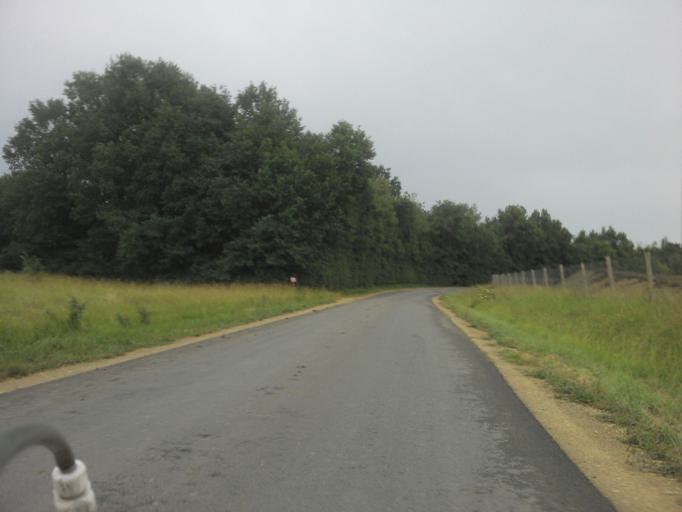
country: FR
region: Pays de la Loire
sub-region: Departement de Maine-et-Loire
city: Breze
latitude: 47.0973
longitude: -0.0023
